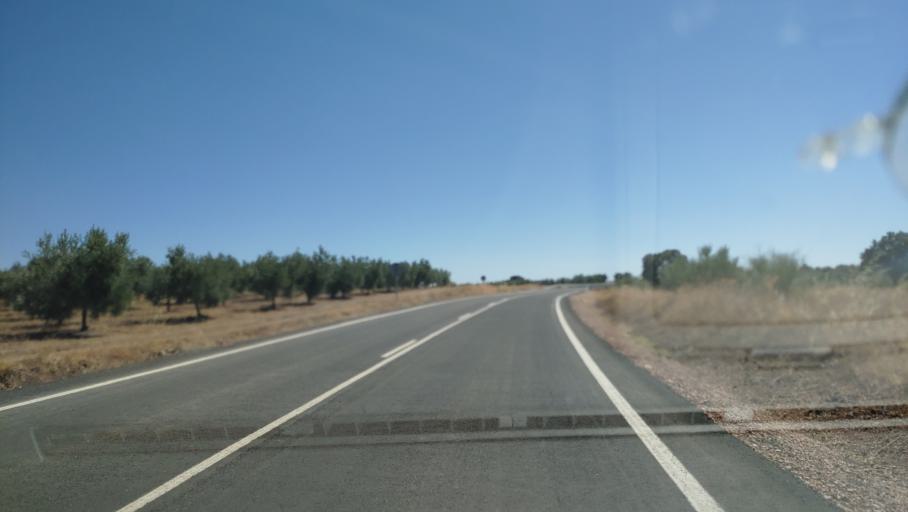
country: ES
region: Castille-La Mancha
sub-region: Provincia de Ciudad Real
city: Albaladejo
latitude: 38.5559
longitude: -2.7794
